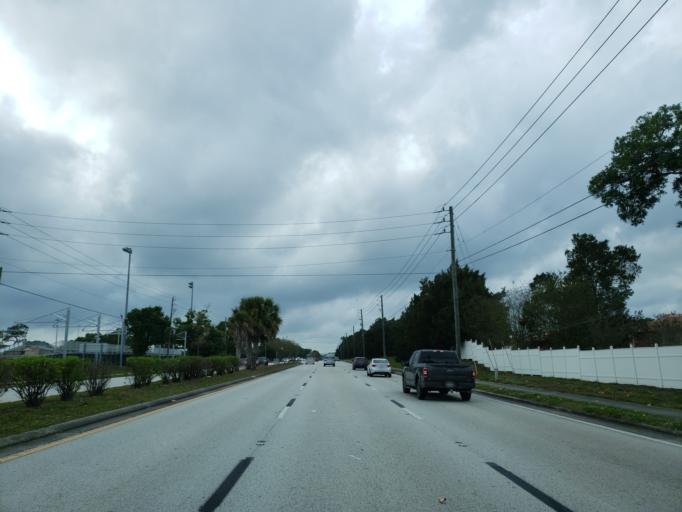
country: US
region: Florida
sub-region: Pinellas County
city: Saint George
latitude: 28.0549
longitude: -82.7023
